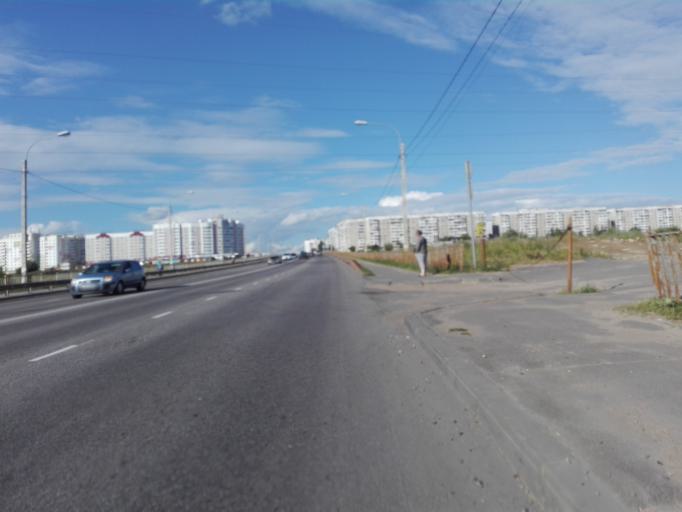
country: RU
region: Orjol
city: Orel
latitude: 53.0080
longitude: 36.1217
